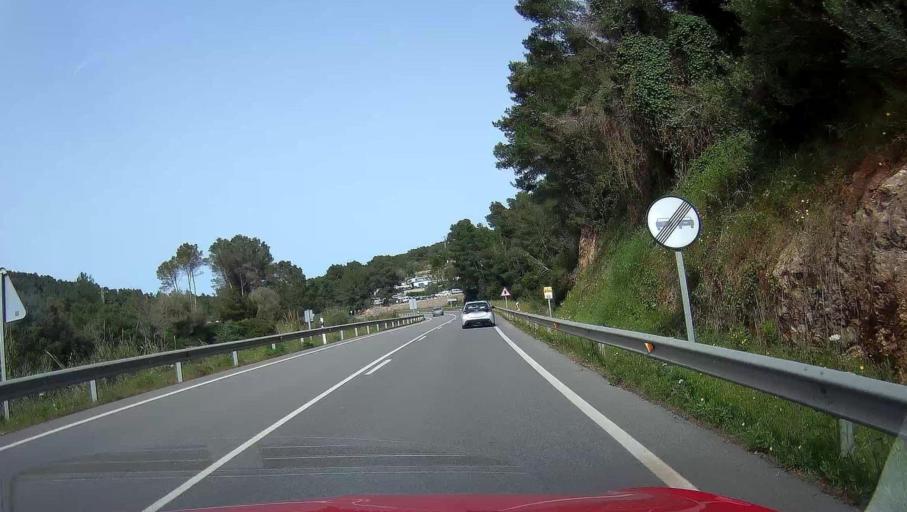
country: ES
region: Balearic Islands
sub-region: Illes Balears
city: Sant Joan de Labritja
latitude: 39.0720
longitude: 1.4977
